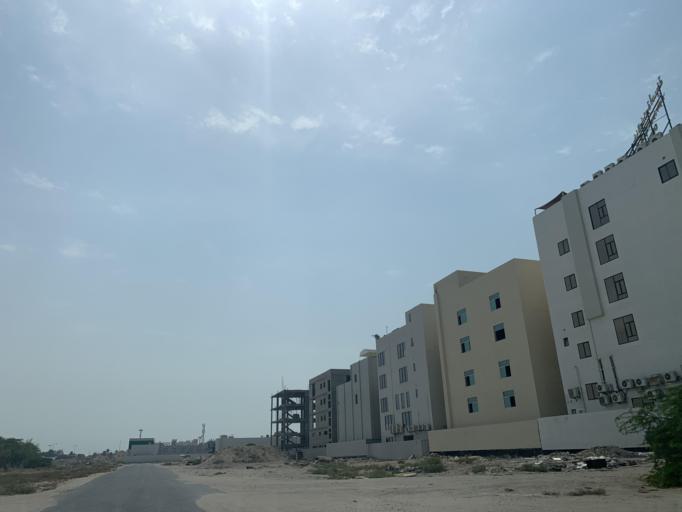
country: BH
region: Manama
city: Jidd Hafs
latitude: 26.2170
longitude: 50.4829
